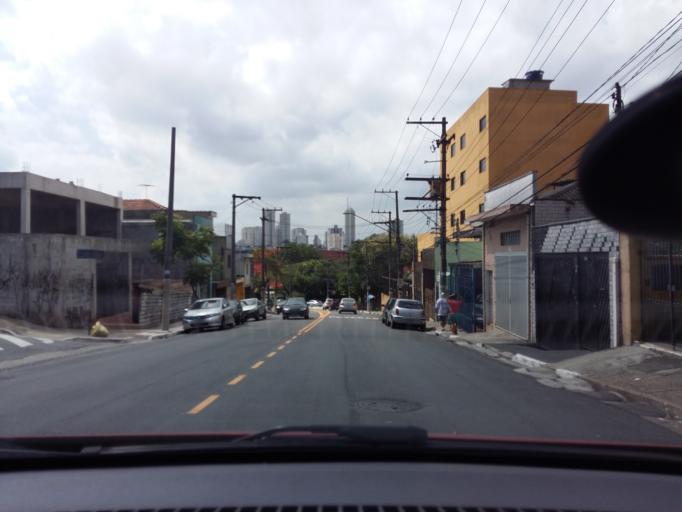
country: BR
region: Sao Paulo
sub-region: Sao Caetano Do Sul
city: Sao Caetano do Sul
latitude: -23.6199
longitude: -46.6085
